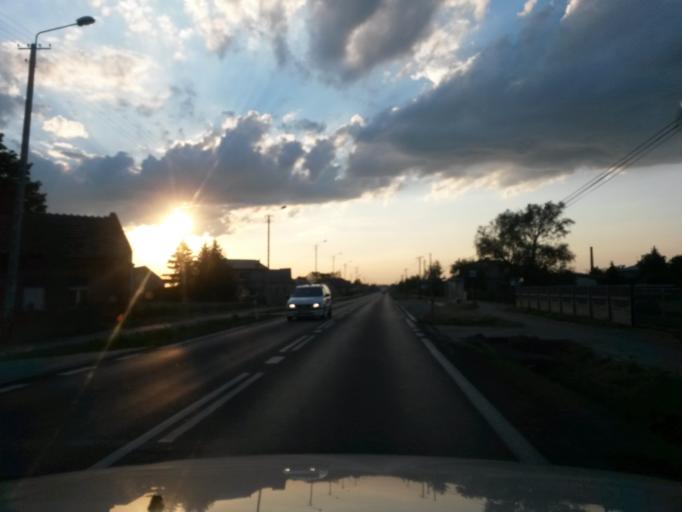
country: PL
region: Lodz Voivodeship
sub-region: Powiat wielunski
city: Wielun
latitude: 51.2318
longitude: 18.5408
